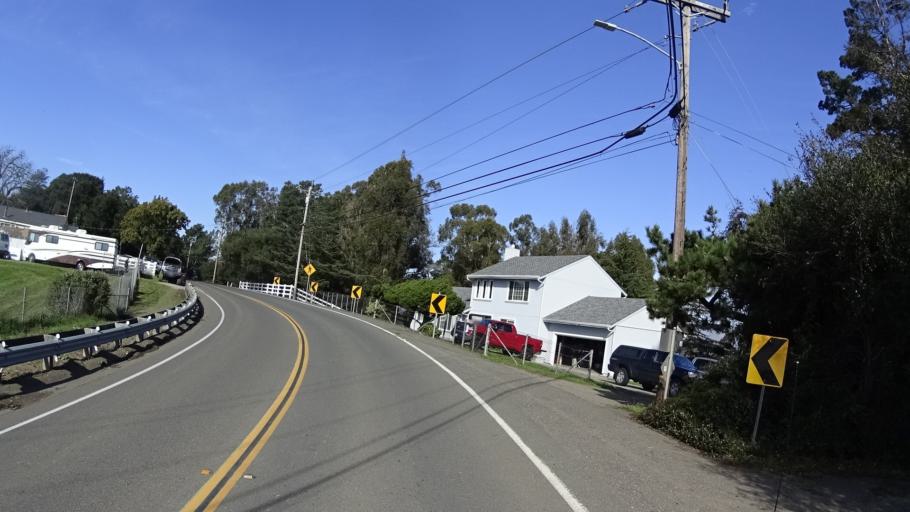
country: US
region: California
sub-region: Alameda County
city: Fairview
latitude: 37.6721
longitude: -122.0291
